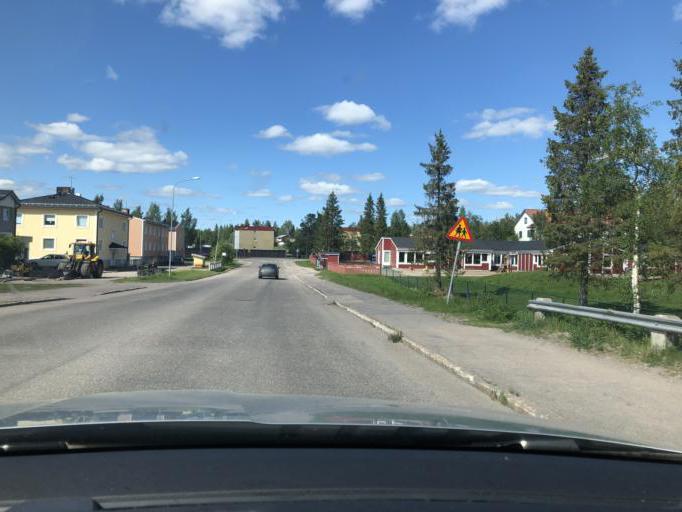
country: SE
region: Norrbotten
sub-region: Gallivare Kommun
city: Gaellivare
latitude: 67.1324
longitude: 20.6822
